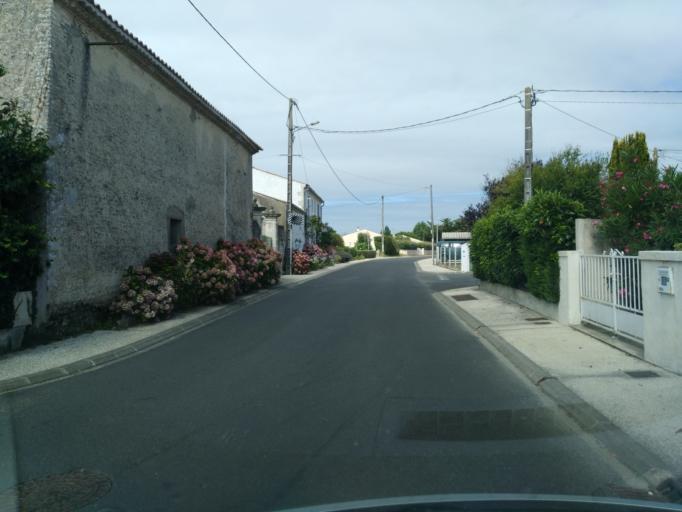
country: FR
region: Poitou-Charentes
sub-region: Departement de la Charente-Maritime
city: Saint-Palais-sur-Mer
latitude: 45.6538
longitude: -1.0816
